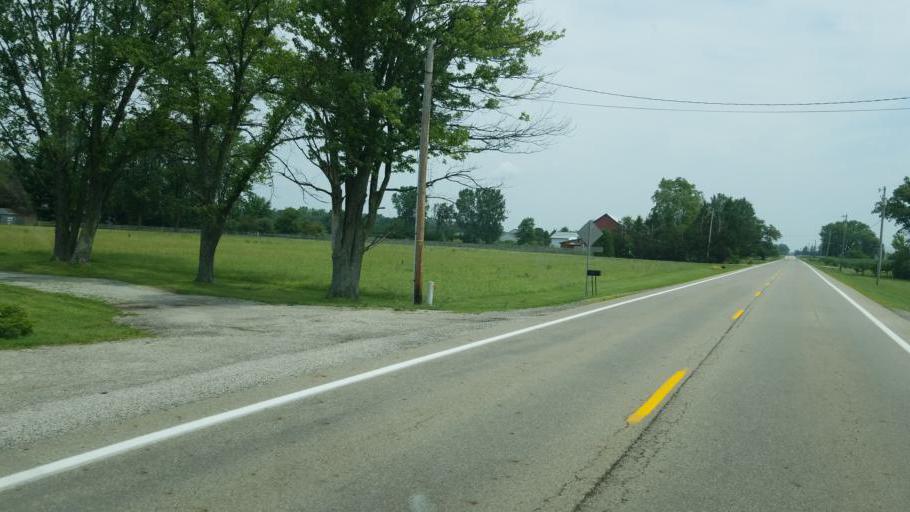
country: US
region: Ohio
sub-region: Madison County
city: West Jefferson
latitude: 39.9901
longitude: -83.3352
